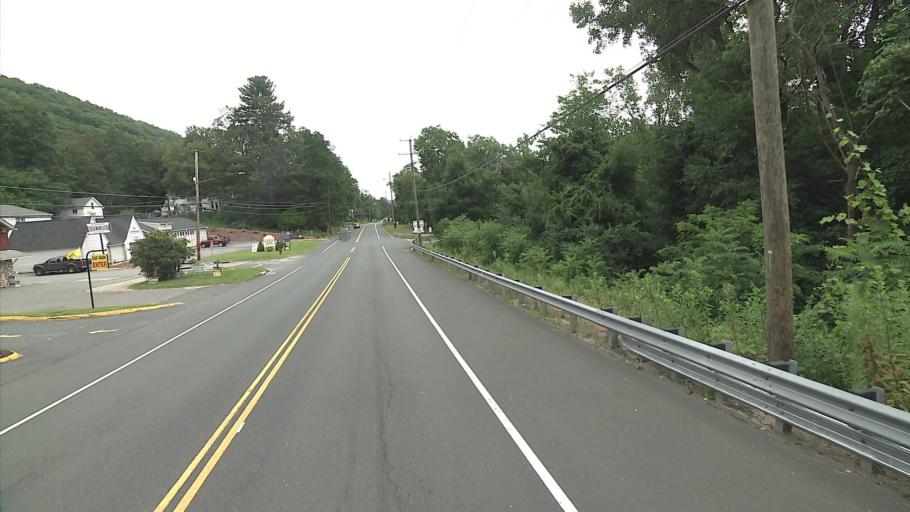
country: US
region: Connecticut
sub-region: Litchfield County
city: Winsted
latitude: 41.9324
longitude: -73.0580
